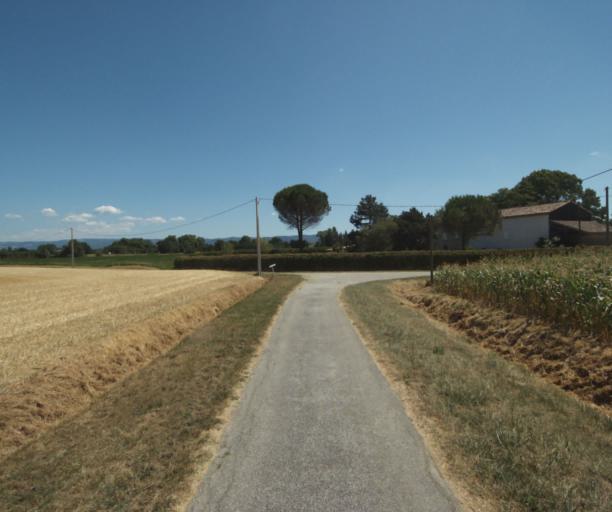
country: FR
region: Midi-Pyrenees
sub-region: Departement de la Haute-Garonne
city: Saint-Felix-Lauragais
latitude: 43.4813
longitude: 1.9378
